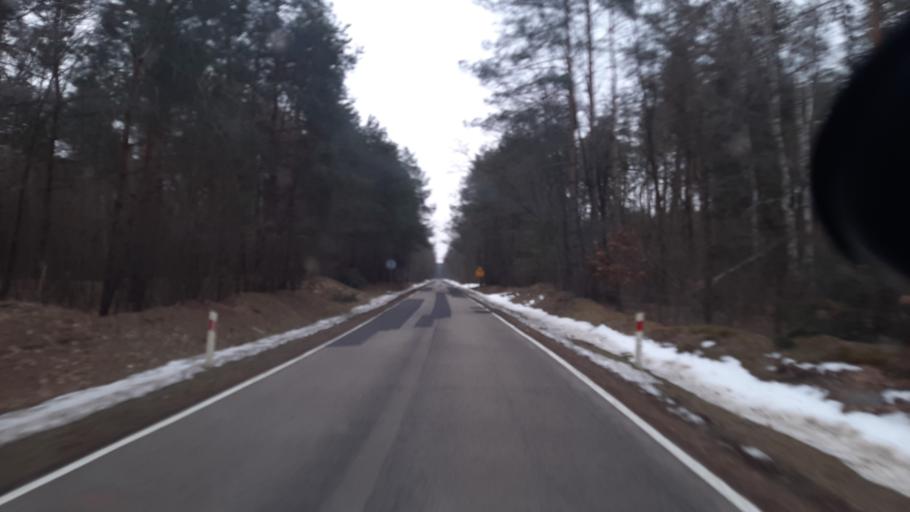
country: PL
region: Lublin Voivodeship
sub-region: Powiat wlodawski
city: Wlodawa
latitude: 51.4910
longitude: 23.5943
